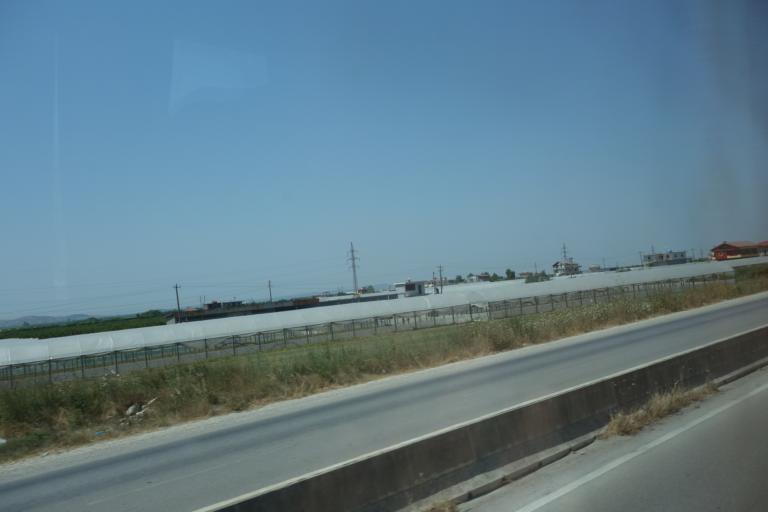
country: AL
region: Fier
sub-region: Rrethi i Lushnjes
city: Golem
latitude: 40.9902
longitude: 19.6689
